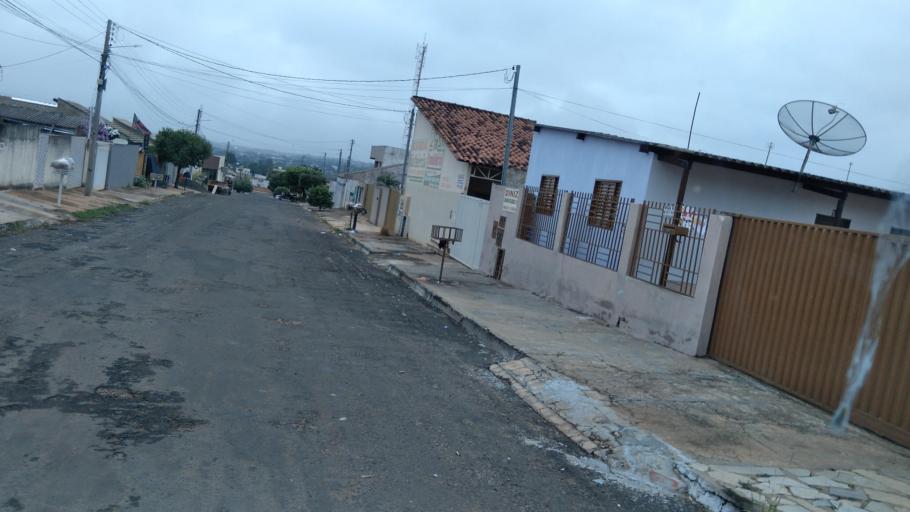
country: BR
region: Goias
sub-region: Mineiros
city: Mineiros
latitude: -17.5747
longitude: -52.5434
